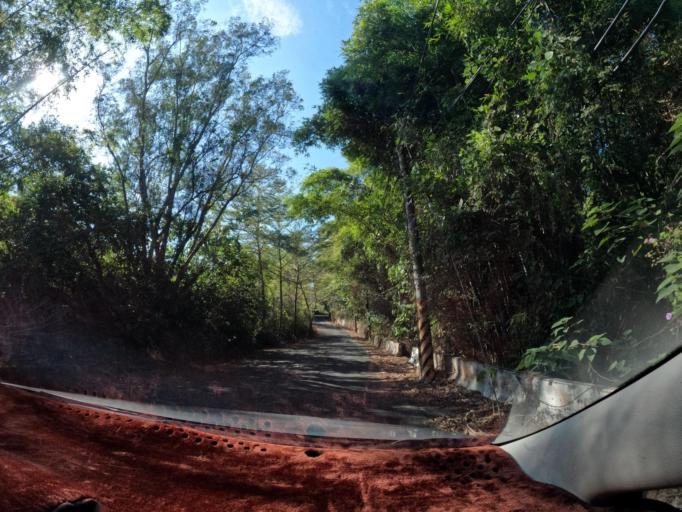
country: TW
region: Taiwan
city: Yujing
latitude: 23.0254
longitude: 120.3887
